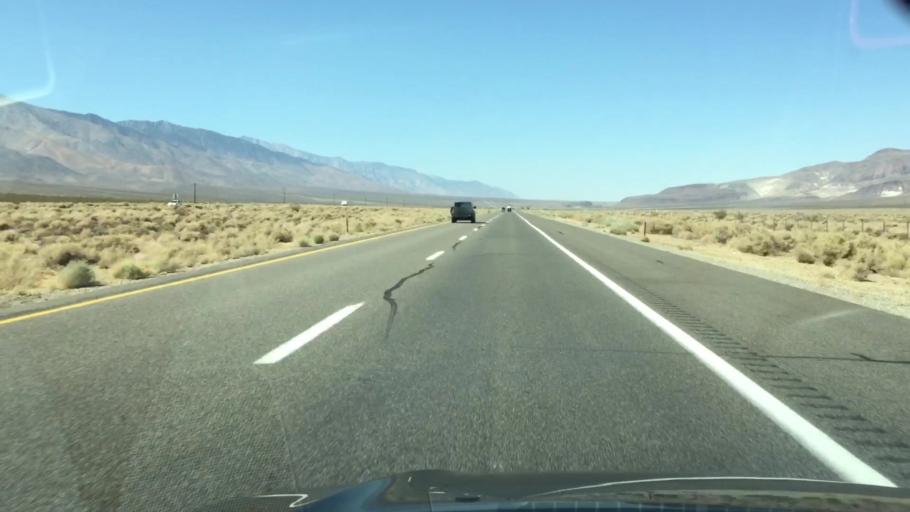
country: US
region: California
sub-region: Kern County
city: Inyokern
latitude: 36.0179
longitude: -117.9383
